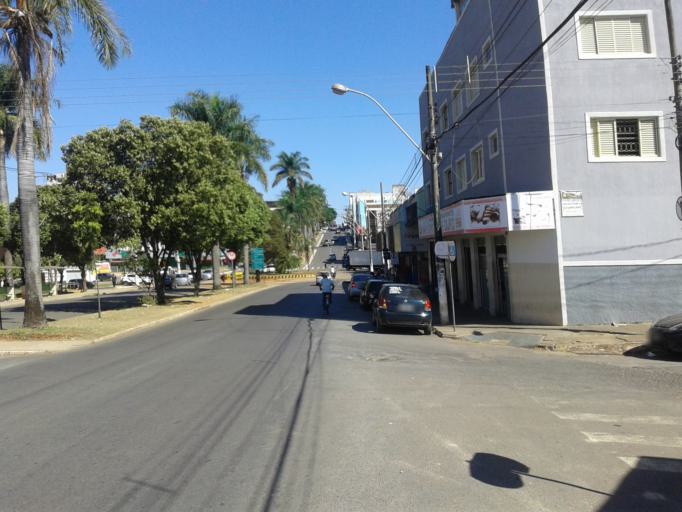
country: BR
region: Minas Gerais
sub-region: Patrocinio
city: Patrocinio
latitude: -18.9388
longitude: -46.9892
